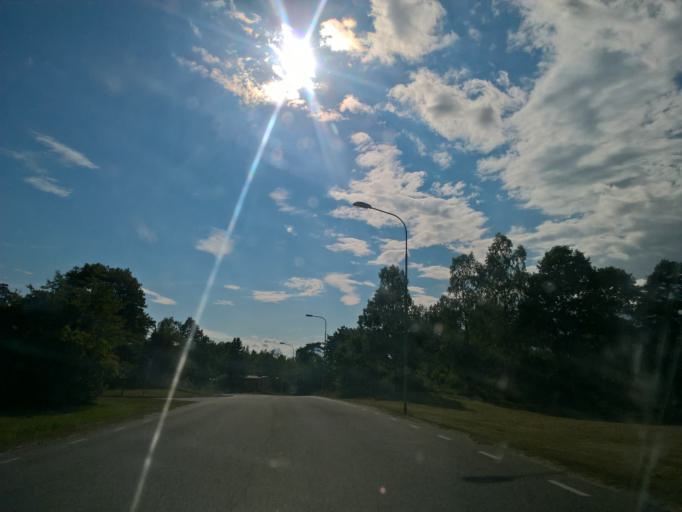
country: SE
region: OEstergoetland
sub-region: Finspangs Kommun
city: Finspang
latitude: 58.7109
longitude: 15.8131
